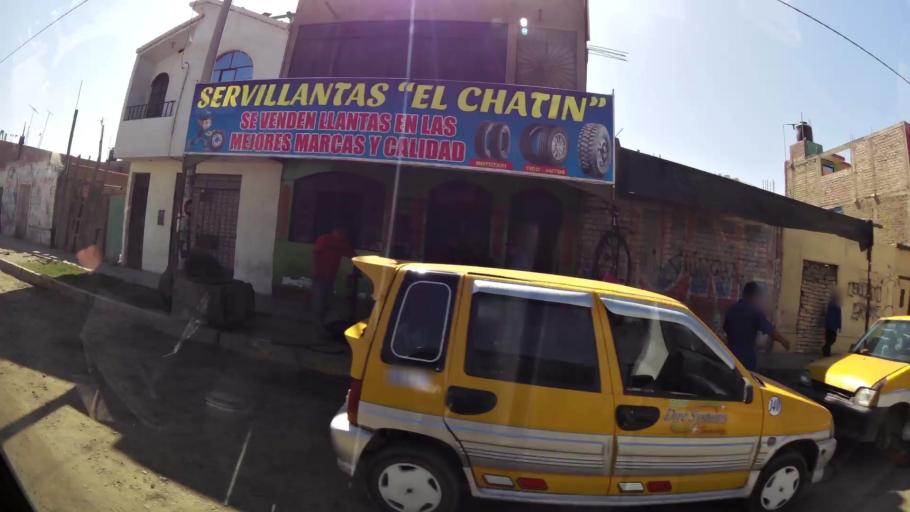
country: PE
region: Ica
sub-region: Provincia de Ica
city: La Tinguina
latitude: -14.0441
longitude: -75.7084
